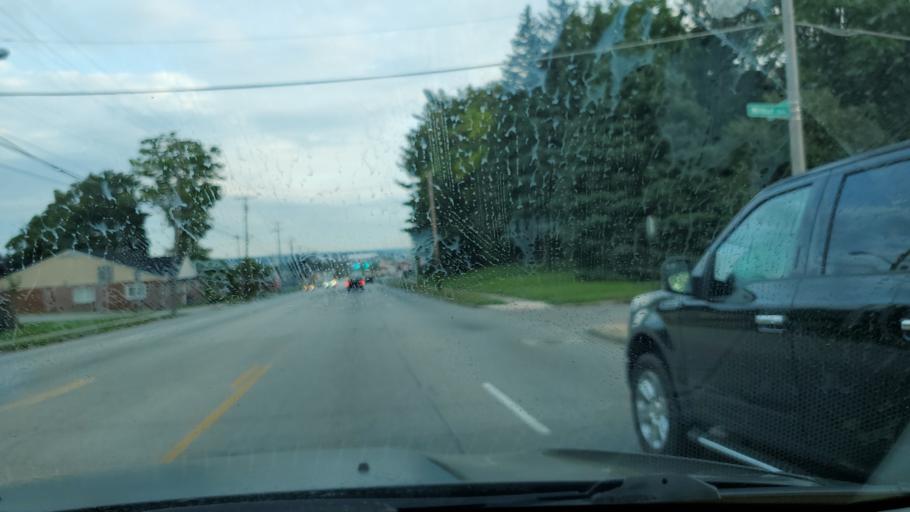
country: US
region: Ohio
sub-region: Mahoning County
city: Youngstown
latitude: 41.0741
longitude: -80.6462
